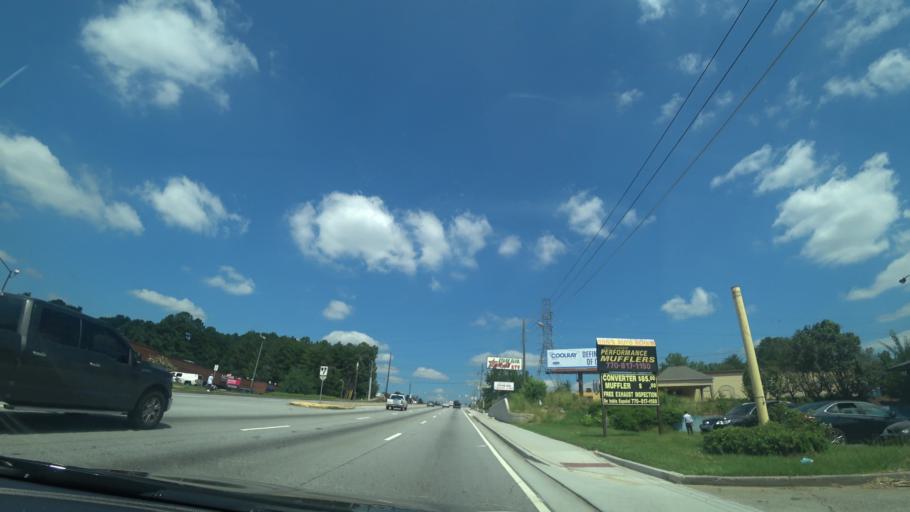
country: US
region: Georgia
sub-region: Gwinnett County
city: Norcross
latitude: 33.9297
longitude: -84.2207
